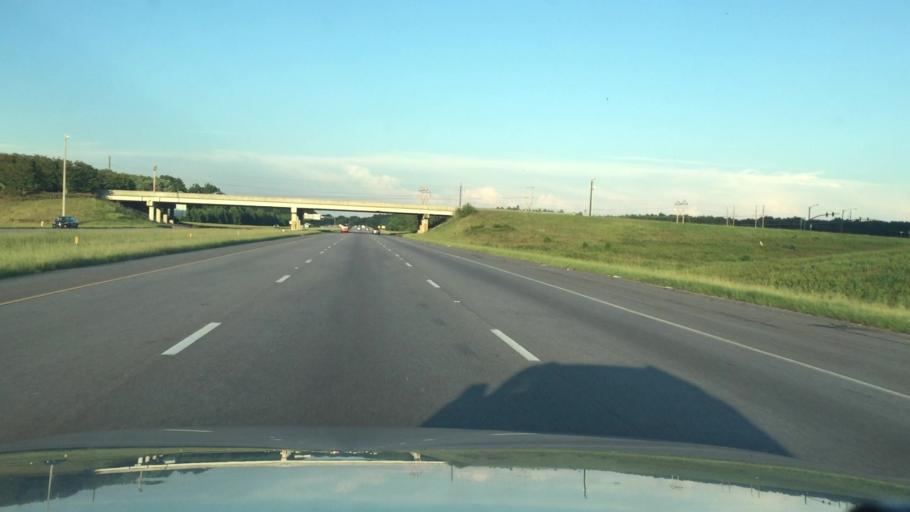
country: US
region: South Carolina
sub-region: Lexington County
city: Cayce
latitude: 33.9290
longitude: -81.0449
